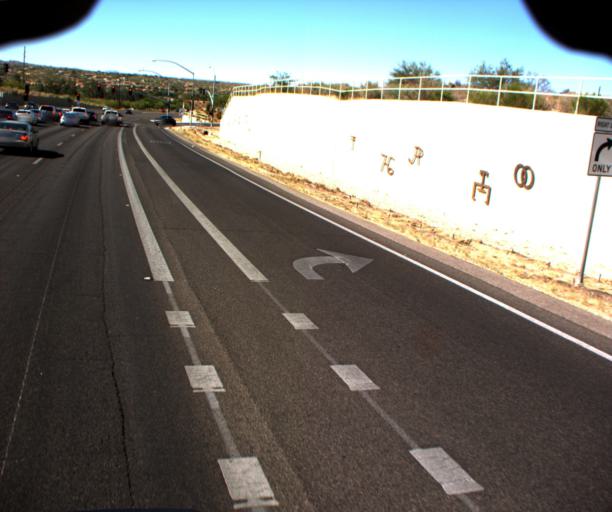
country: US
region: Arizona
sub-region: Pima County
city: Oro Valley
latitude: 32.3870
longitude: -110.9643
